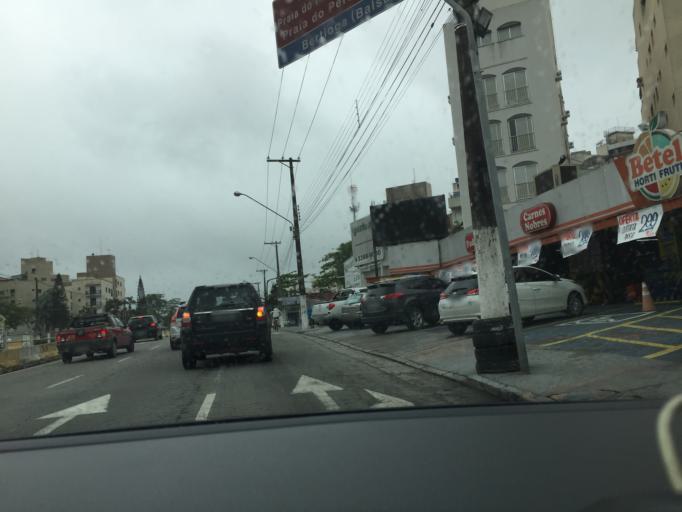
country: BR
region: Sao Paulo
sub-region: Guaruja
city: Guaruja
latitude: -23.9804
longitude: -46.2262
